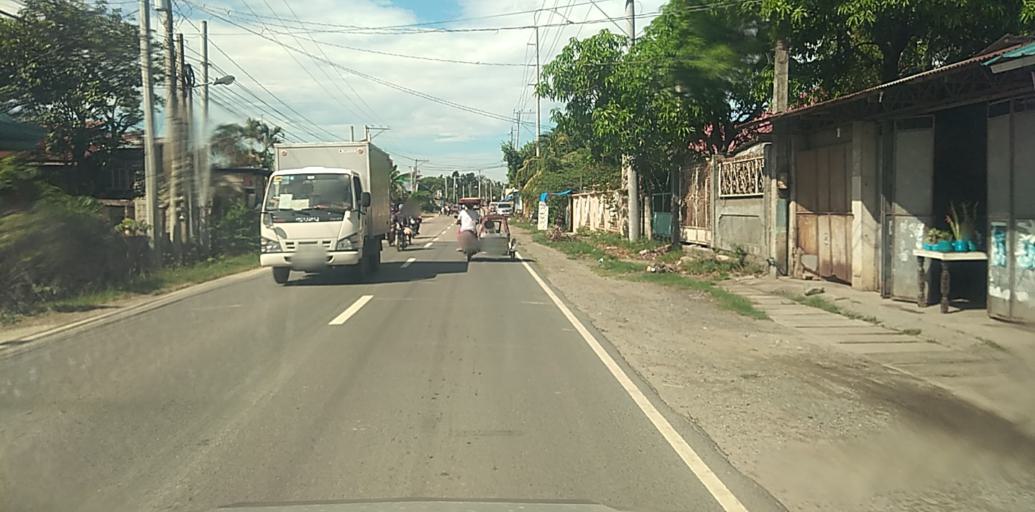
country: PH
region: Central Luzon
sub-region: Province of Pampanga
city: Arayat
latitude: 15.1477
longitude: 120.7610
